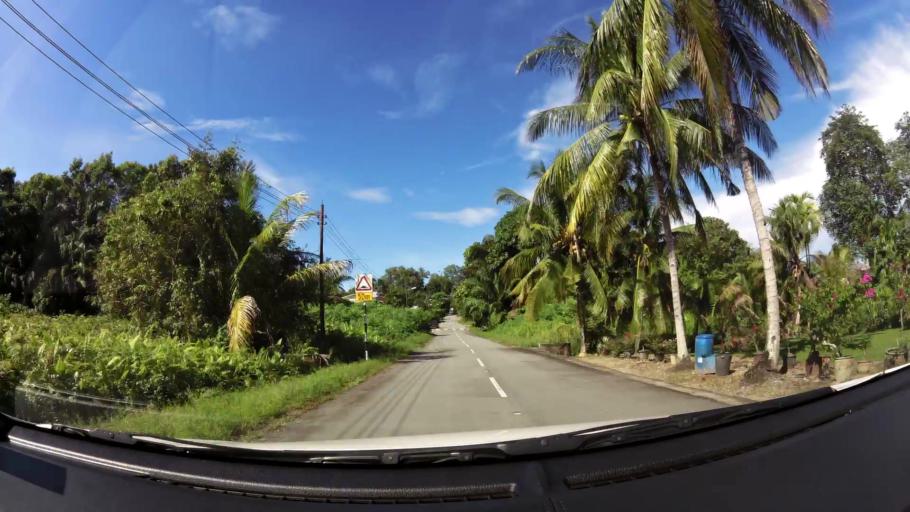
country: BN
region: Brunei and Muara
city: Bandar Seri Begawan
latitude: 4.9665
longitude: 114.9274
